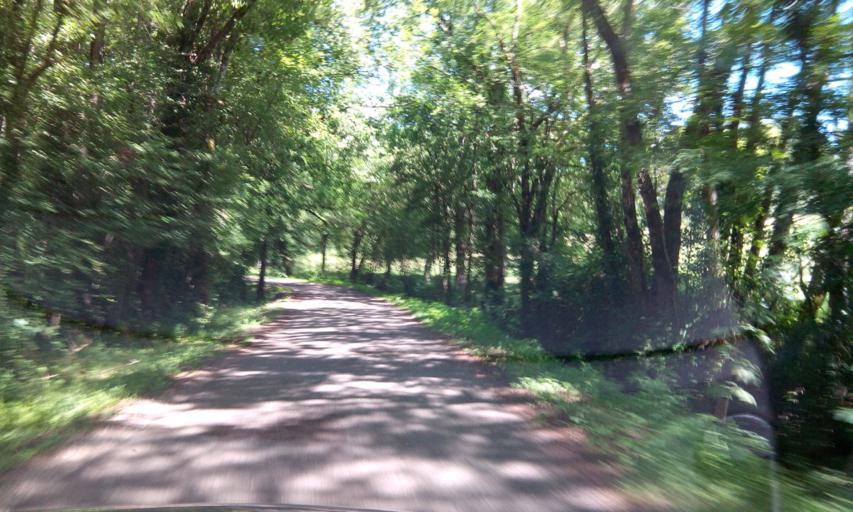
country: FR
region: Limousin
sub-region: Departement de la Correze
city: Meyssac
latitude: 45.0616
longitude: 1.6050
